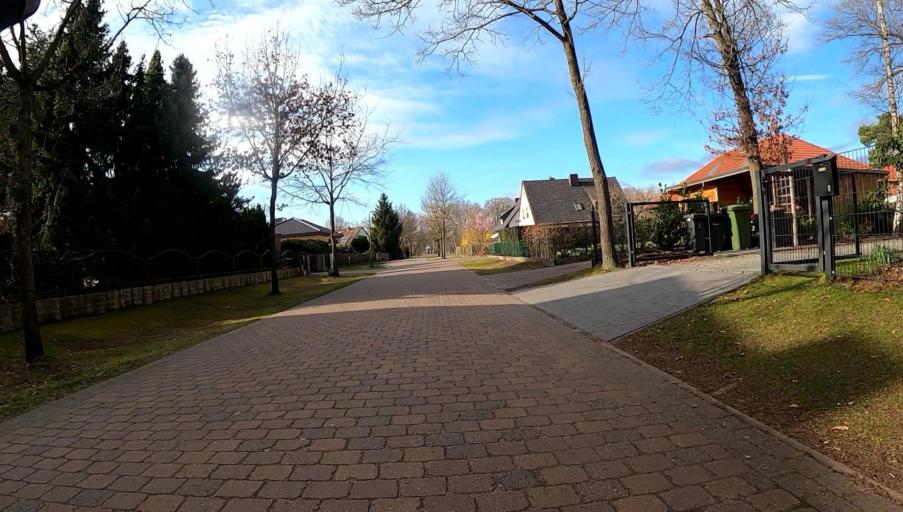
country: DE
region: Lower Saxony
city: Lindwedel
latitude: 52.6074
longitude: 9.6611
